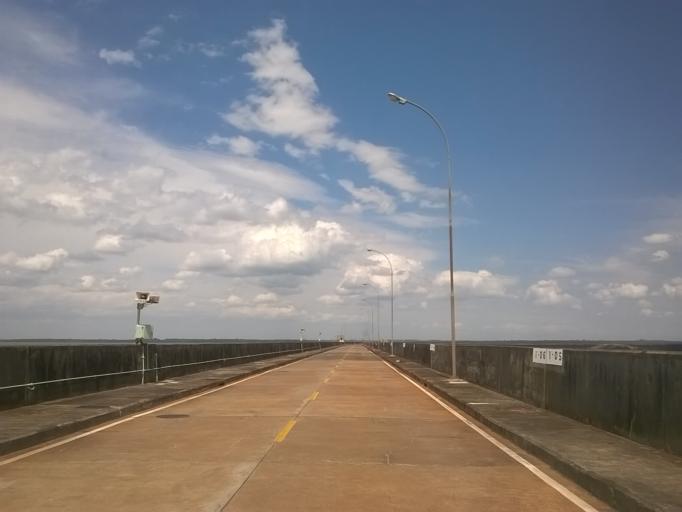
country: PY
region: Alto Parana
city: Ciudad del Este
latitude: -25.4084
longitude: -54.5838
